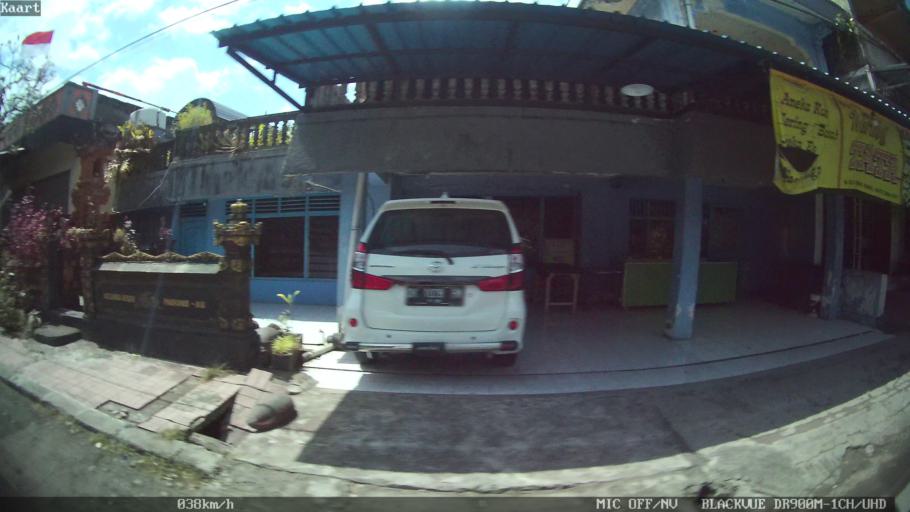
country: ID
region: Bali
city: Denpasar
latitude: -8.6552
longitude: 115.1862
